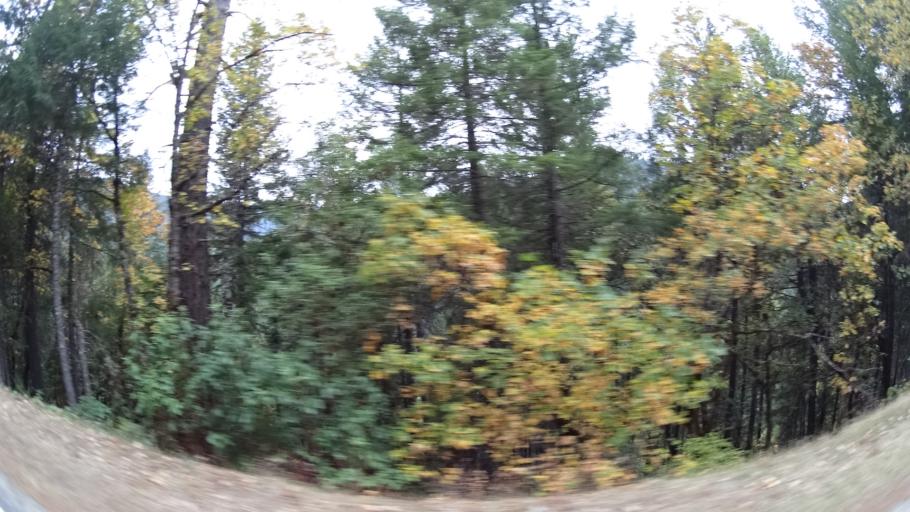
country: US
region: California
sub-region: Siskiyou County
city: Happy Camp
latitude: 41.8113
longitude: -123.3829
